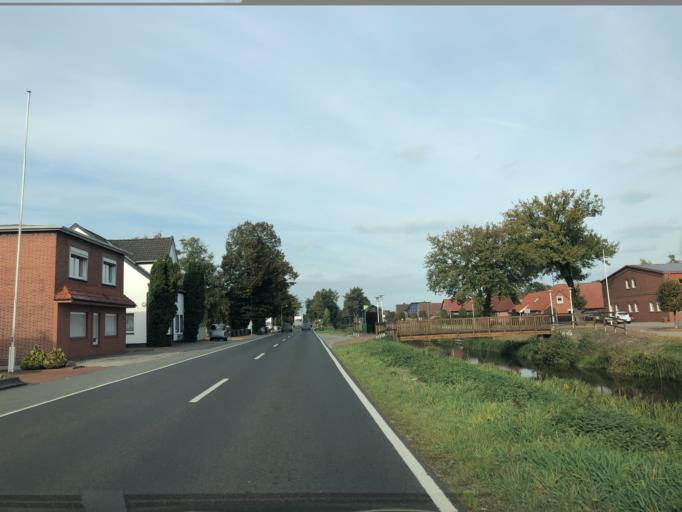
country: DE
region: Lower Saxony
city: Surwold
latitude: 53.0169
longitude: 7.4854
